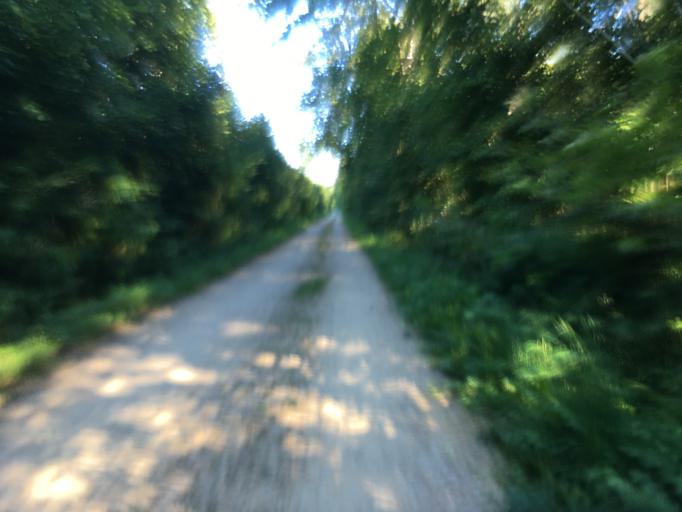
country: CH
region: Fribourg
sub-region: See District
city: Bas-Vully
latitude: 46.9515
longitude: 7.1305
